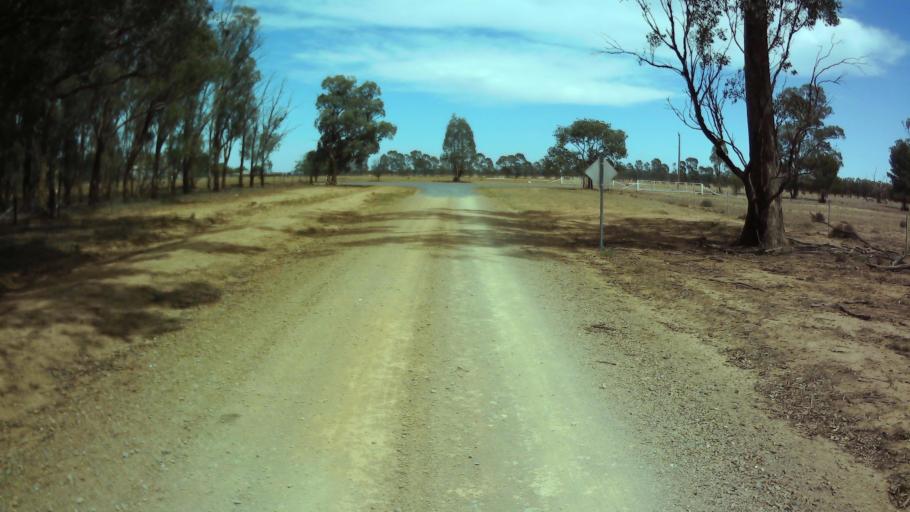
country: AU
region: New South Wales
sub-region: Weddin
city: Grenfell
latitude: -33.8563
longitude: 147.9045
